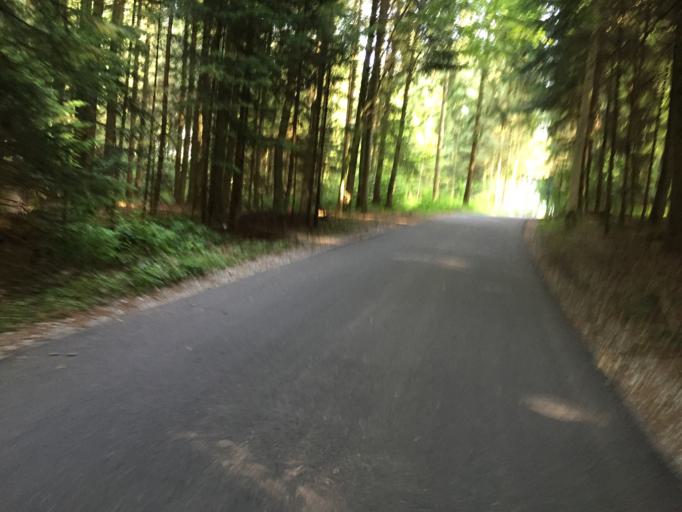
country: CH
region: Bern
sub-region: Bern-Mittelland District
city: Rubigen
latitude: 46.9232
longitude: 7.5205
